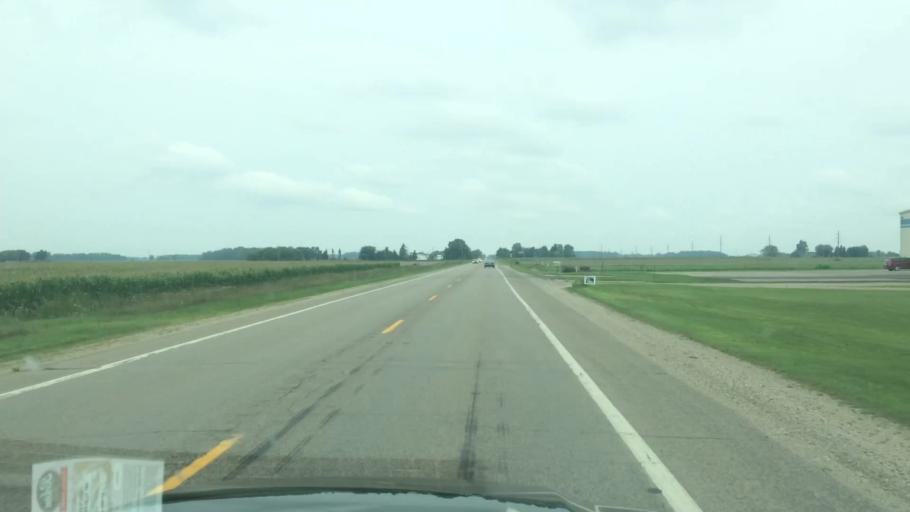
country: US
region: Michigan
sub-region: Huron County
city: Bad Axe
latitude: 43.8434
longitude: -83.0016
